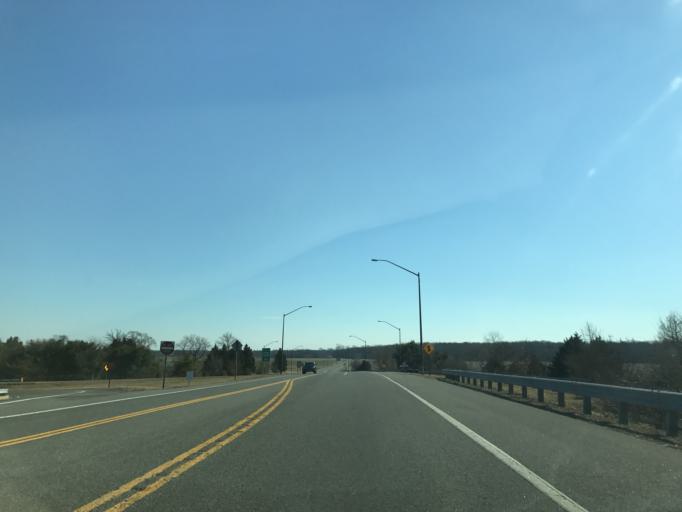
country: US
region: Maryland
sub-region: Queen Anne's County
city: Centreville
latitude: 39.0141
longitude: -76.0763
